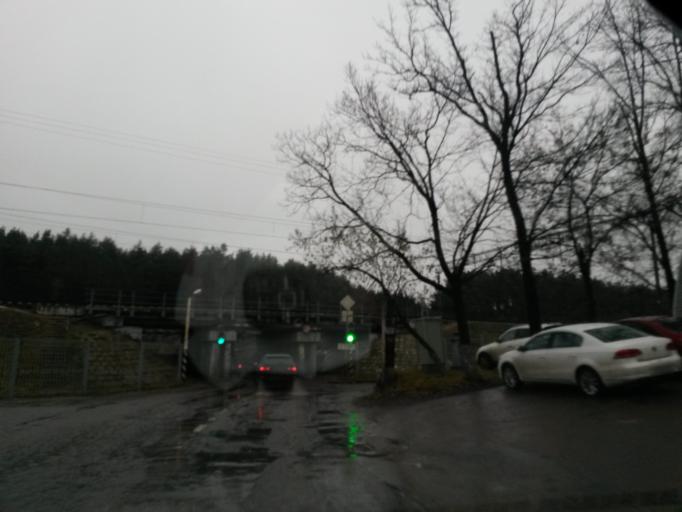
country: RU
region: Moskovskaya
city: Zarech'ye
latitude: 55.6619
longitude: 37.4085
